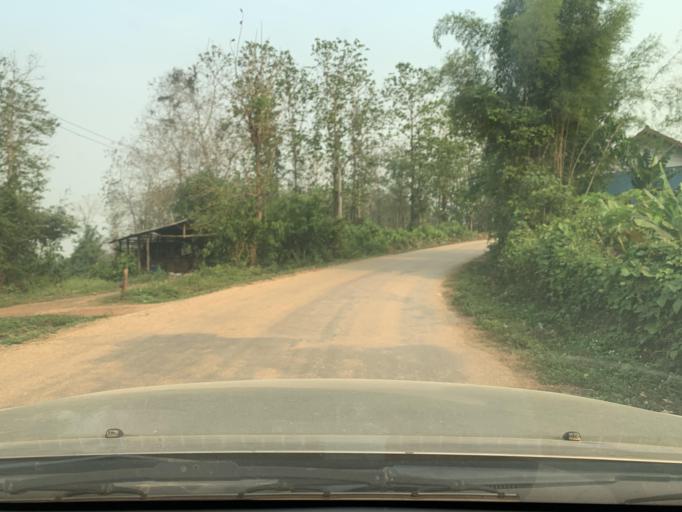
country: LA
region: Louangphabang
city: Louangphabang
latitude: 19.9144
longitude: 102.0768
